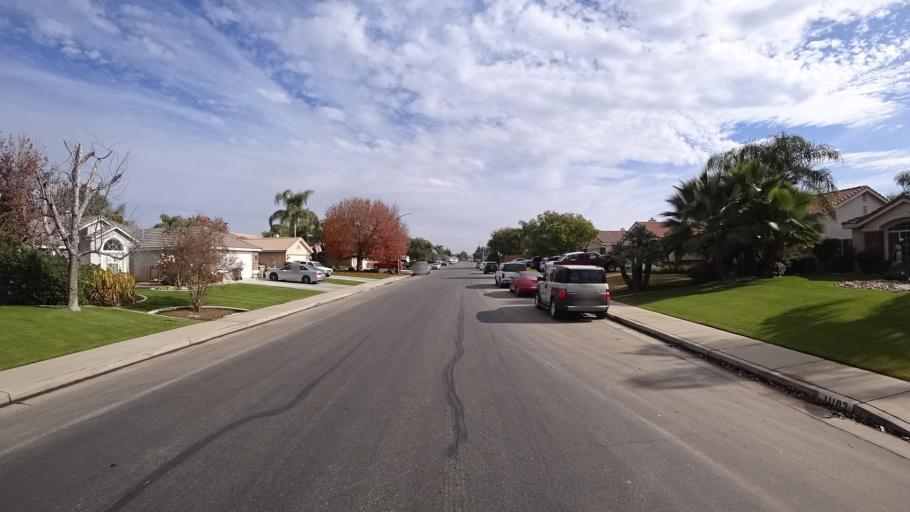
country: US
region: California
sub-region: Kern County
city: Greenacres
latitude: 35.4002
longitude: -119.1258
